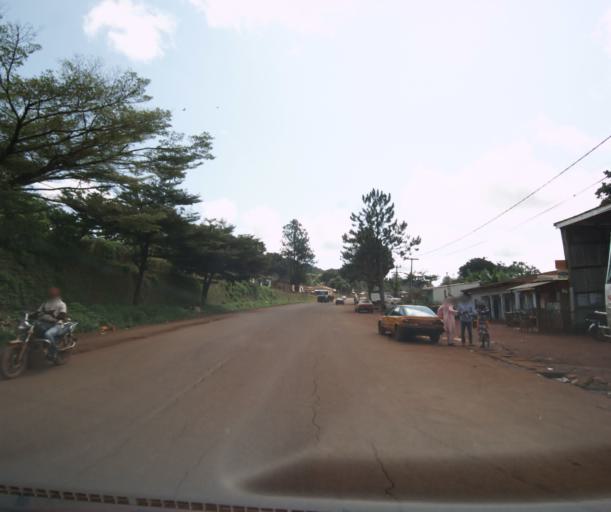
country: CM
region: West
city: Foumban
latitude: 5.7303
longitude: 10.8728
